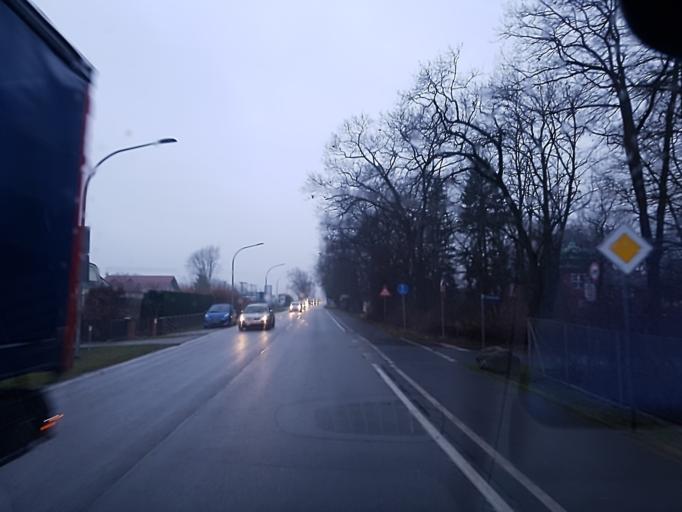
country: DE
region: Brandenburg
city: Luebben
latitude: 51.9318
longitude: 13.8839
